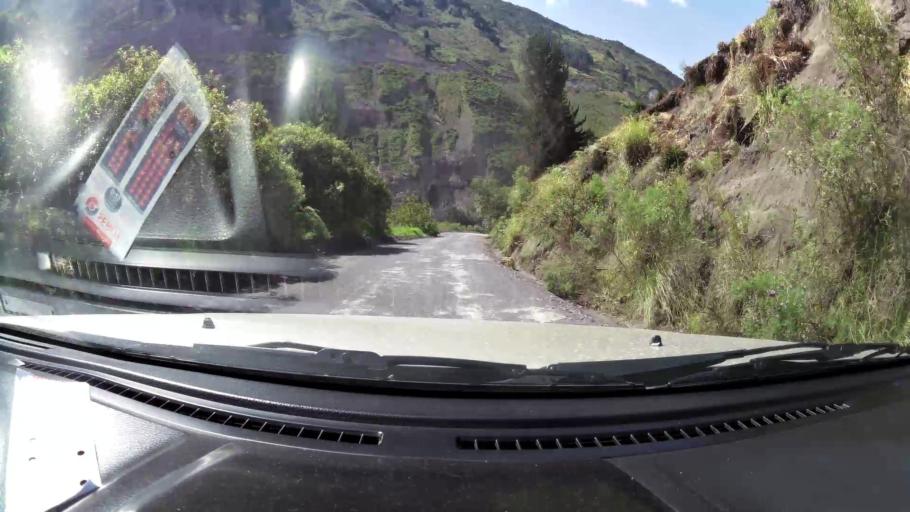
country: EC
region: Tungurahua
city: Banos
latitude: -1.4822
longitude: -78.5127
